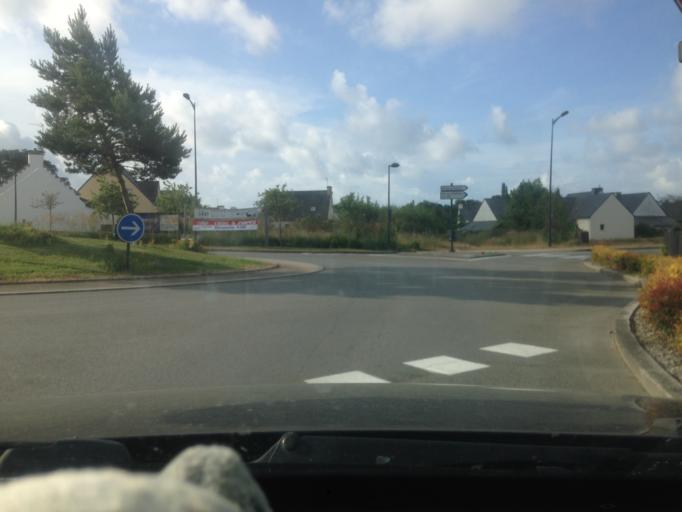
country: FR
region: Brittany
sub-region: Departement du Morbihan
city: Carnac
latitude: 47.5882
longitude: -3.0906
